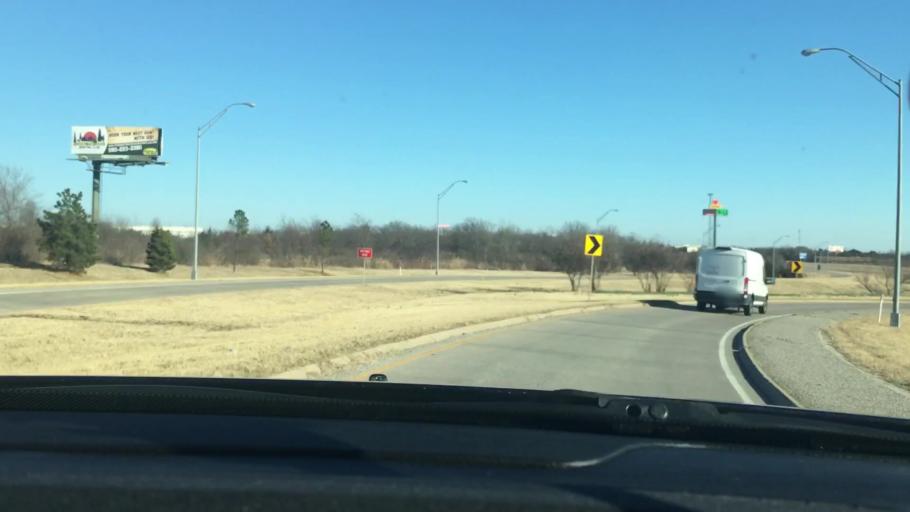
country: US
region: Oklahoma
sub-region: Carter County
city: Ardmore
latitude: 34.1885
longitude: -97.1686
